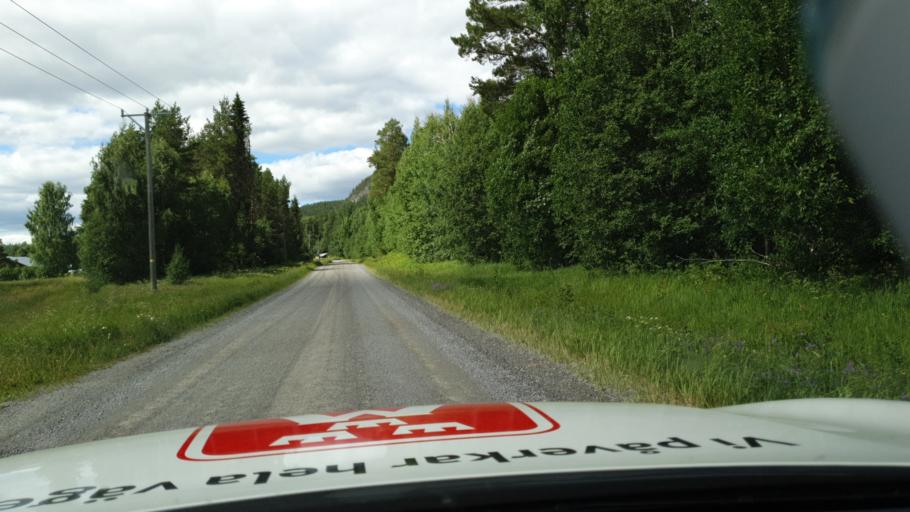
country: SE
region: Jaemtland
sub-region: Braecke Kommun
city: Braecke
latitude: 63.2054
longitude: 15.4069
